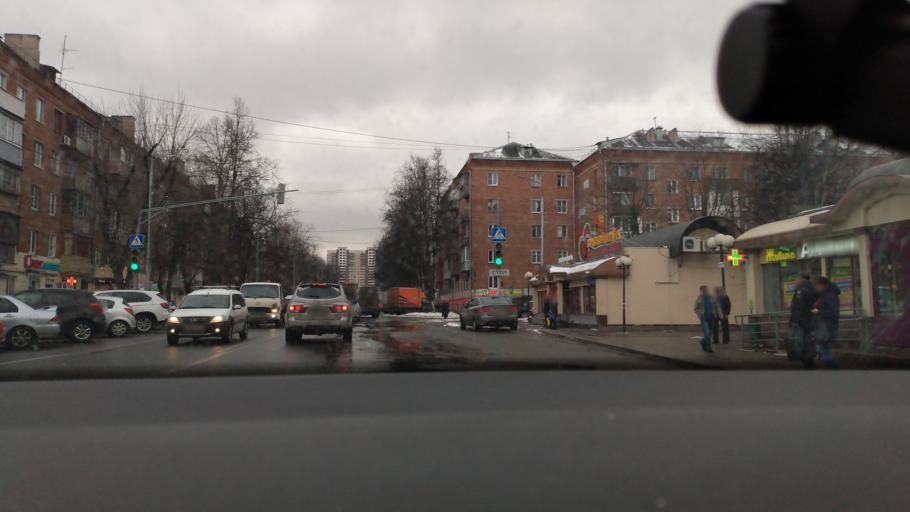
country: RU
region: Moskovskaya
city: Balashikha
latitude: 55.8001
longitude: 37.9347
